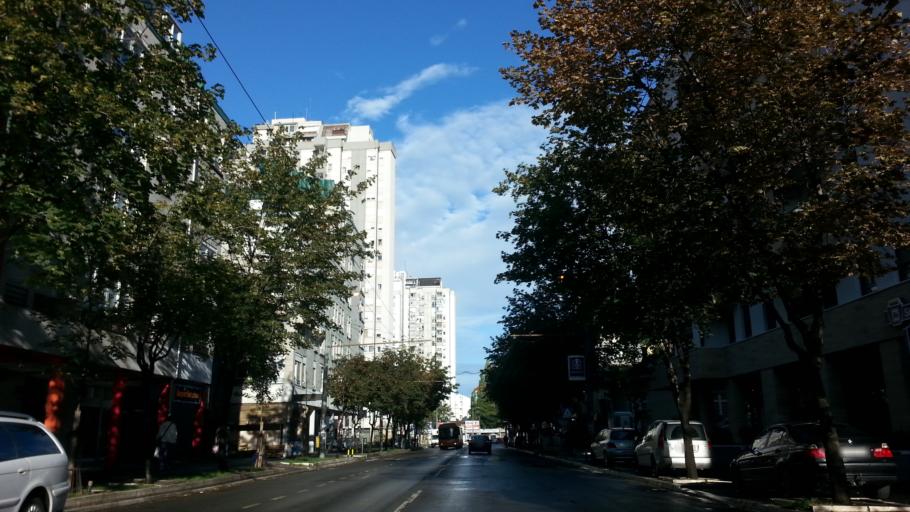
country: RS
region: Central Serbia
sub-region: Belgrade
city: Vracar
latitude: 44.7945
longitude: 20.4924
